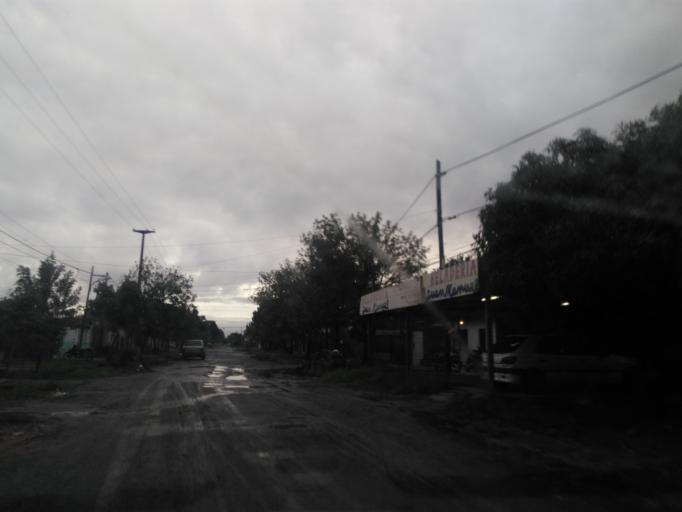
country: AR
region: Chaco
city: Resistencia
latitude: -27.4689
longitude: -59.0028
